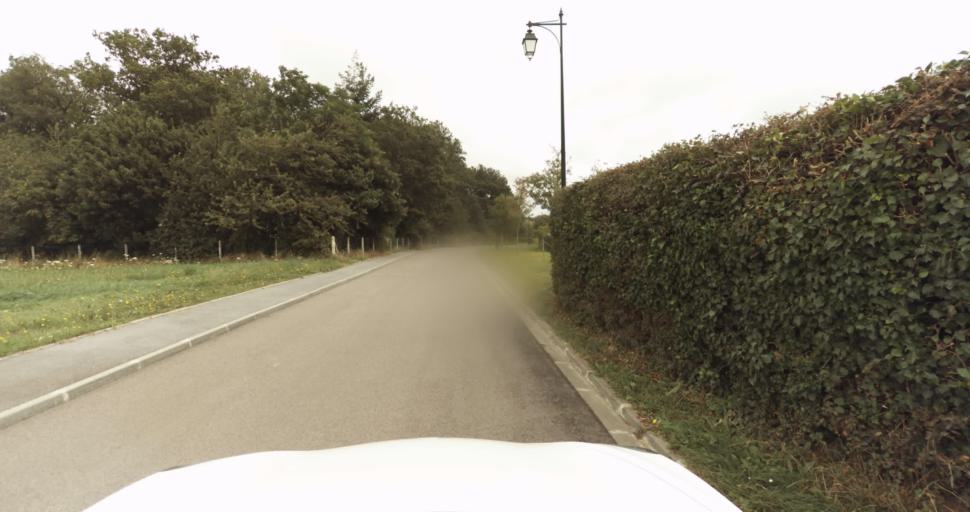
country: FR
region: Haute-Normandie
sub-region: Departement de l'Eure
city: Claville
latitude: 49.0275
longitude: 1.0423
